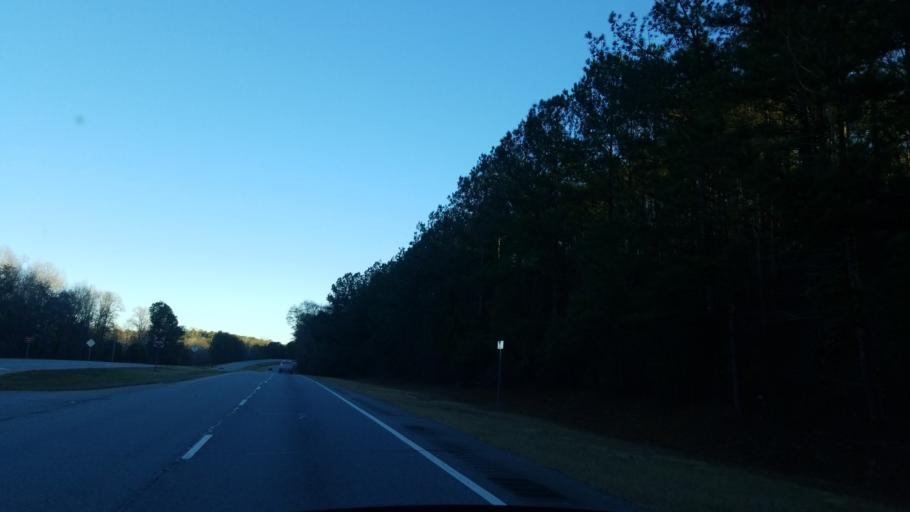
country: US
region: Georgia
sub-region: Chattahoochee County
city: Cusseta
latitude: 32.2640
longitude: -84.7390
